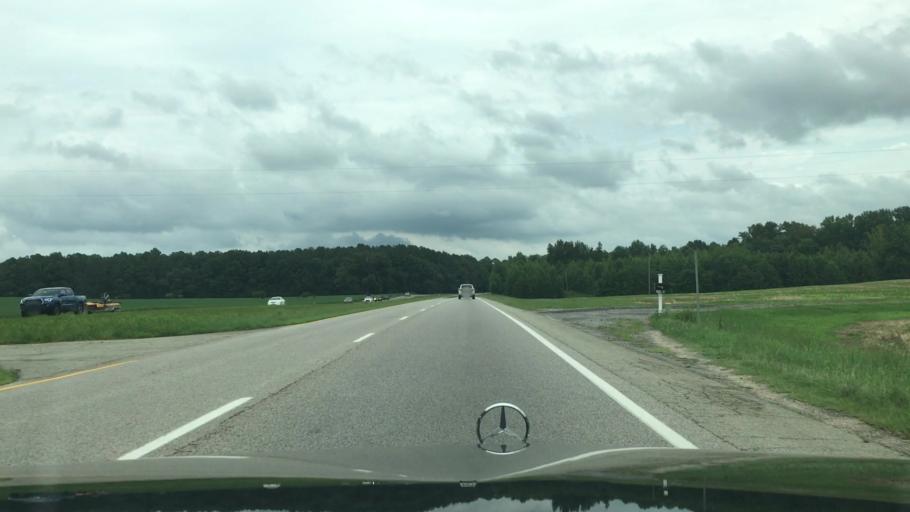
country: US
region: Virginia
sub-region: Amelia County
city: Amelia Court House
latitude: 37.3577
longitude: -77.8700
